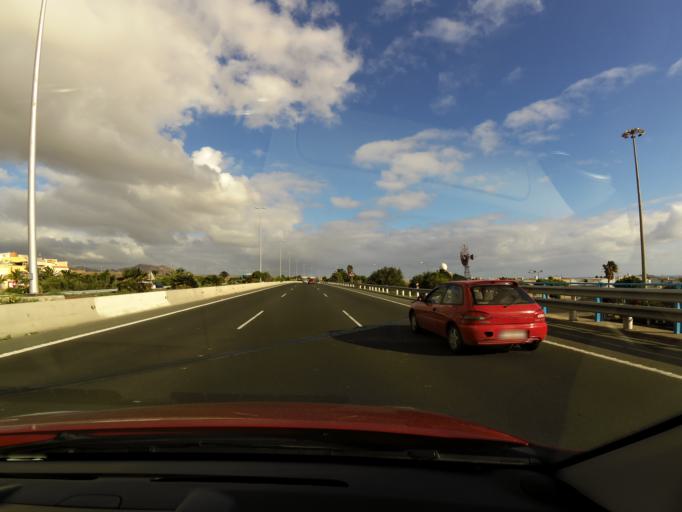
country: ES
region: Canary Islands
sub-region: Provincia de Las Palmas
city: Ingenio
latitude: 27.9201
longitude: -15.3980
